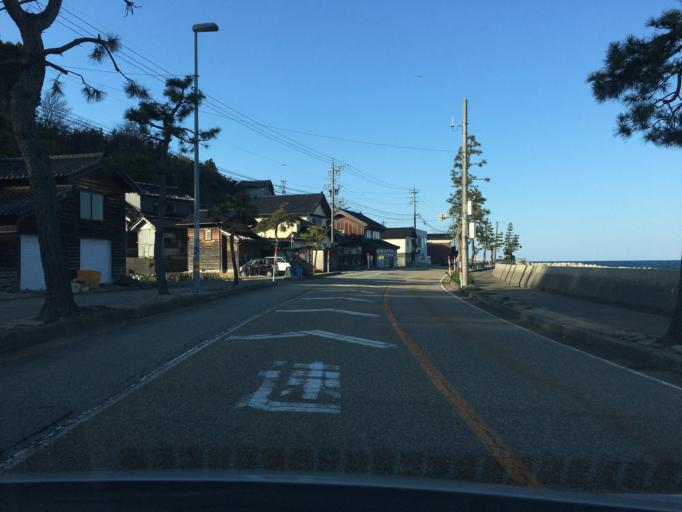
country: JP
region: Ishikawa
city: Nanao
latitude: 36.9665
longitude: 137.0557
